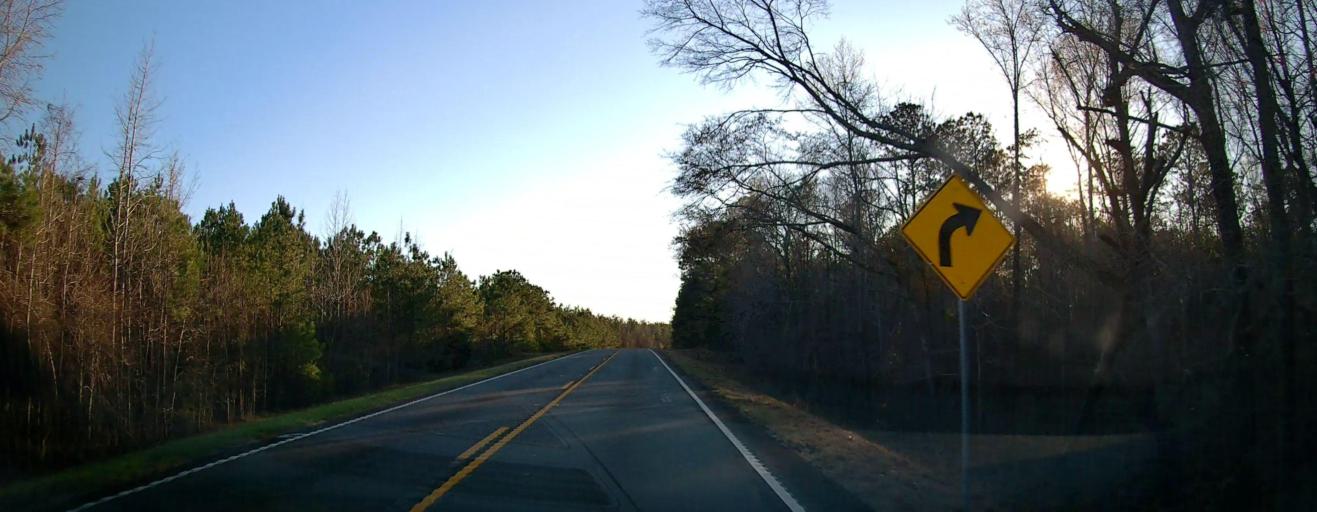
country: US
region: Georgia
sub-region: Talbot County
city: Talbotton
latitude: 32.6513
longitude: -84.6733
